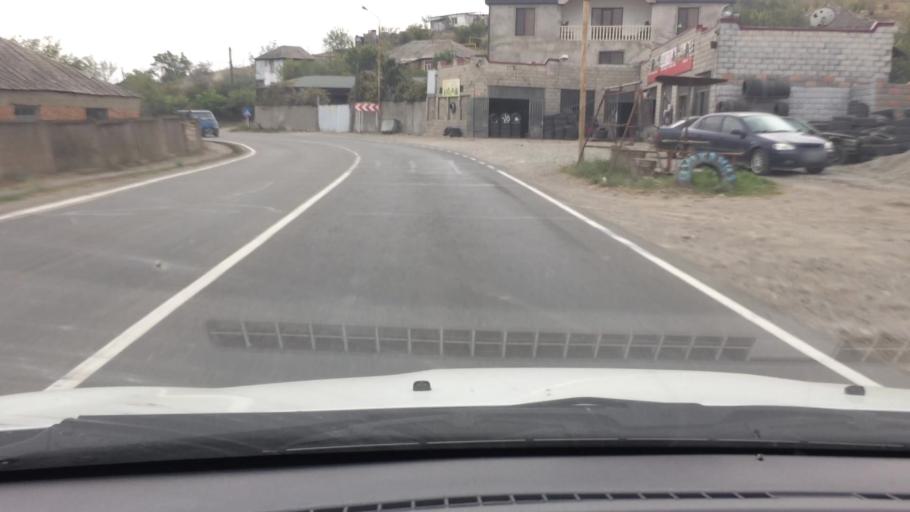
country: GE
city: Naghvarevi
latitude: 41.3685
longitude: 44.8379
